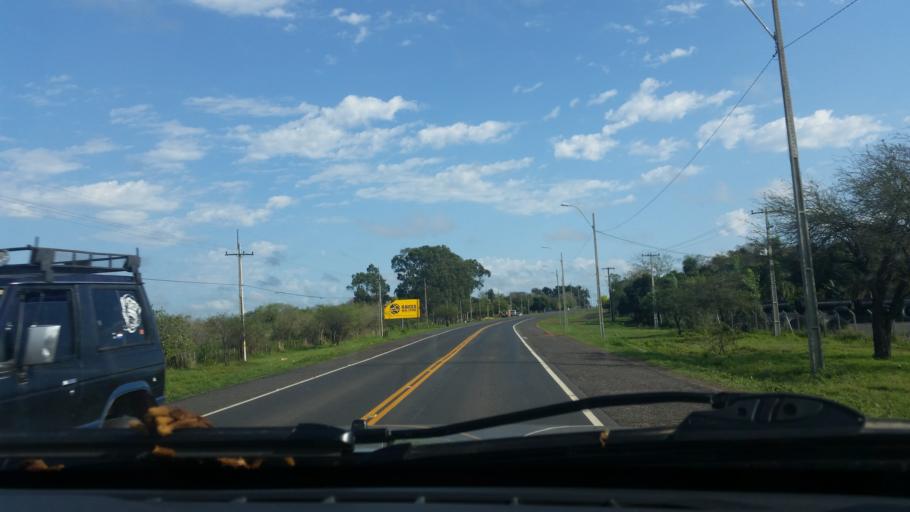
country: PY
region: Presidente Hayes
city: Villa Hayes
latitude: -25.0445
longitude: -57.5450
